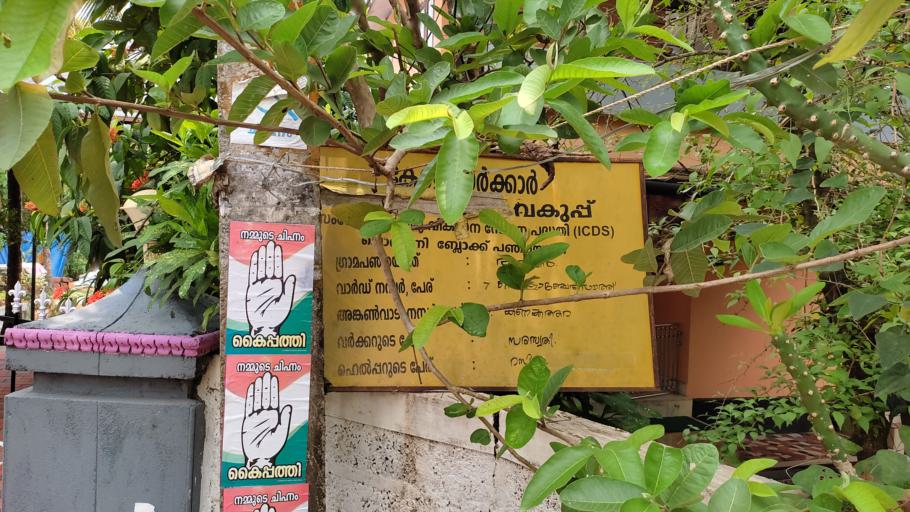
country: IN
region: Kerala
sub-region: Malappuram
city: Tirur
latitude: 10.8466
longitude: 76.0081
